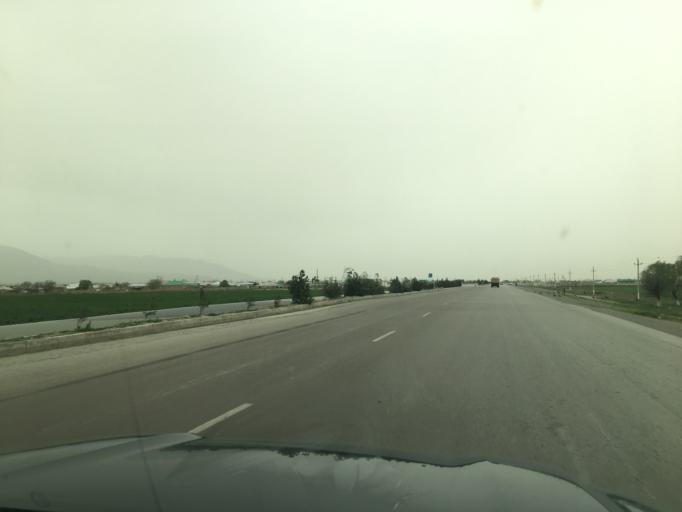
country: TM
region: Ahal
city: Baharly
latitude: 38.3921
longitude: 57.4841
